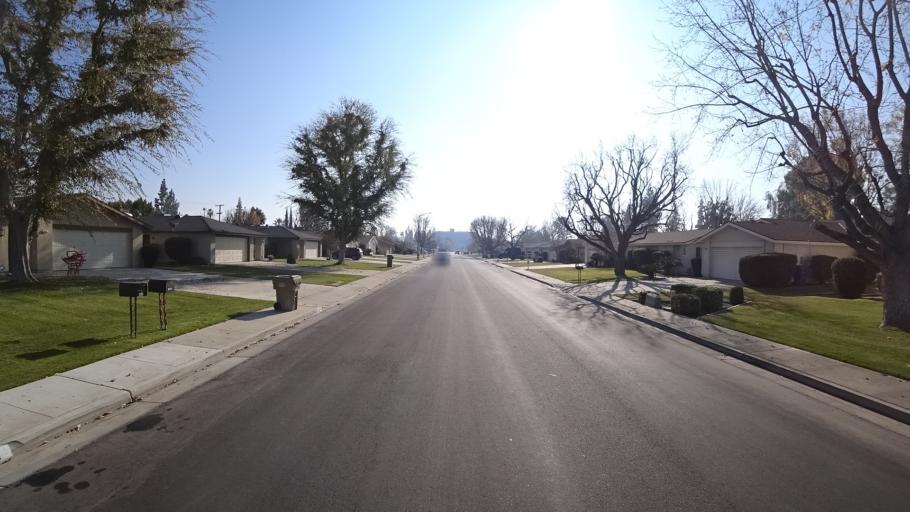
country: US
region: California
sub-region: Kern County
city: Bakersfield
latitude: 35.3476
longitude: -119.0624
